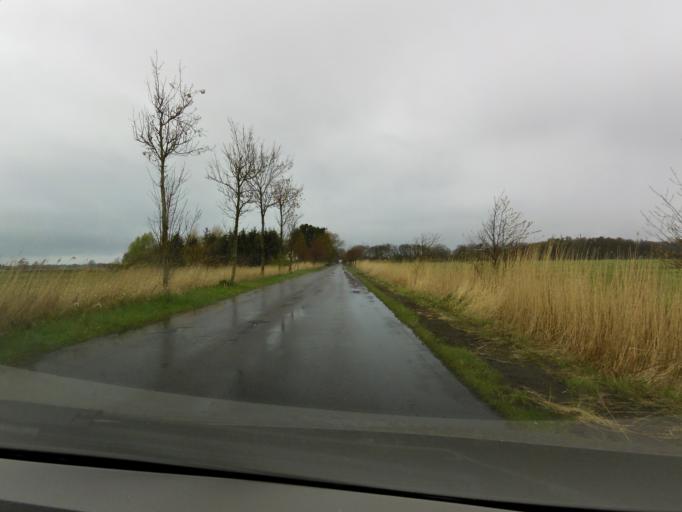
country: DE
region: Mecklenburg-Vorpommern
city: Zingst
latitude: 54.4311
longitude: 12.7346
